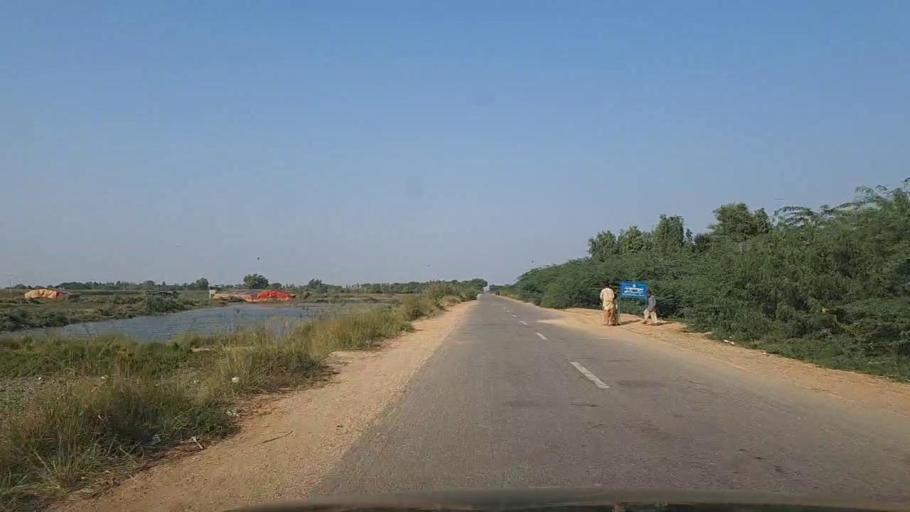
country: PK
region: Sindh
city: Thatta
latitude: 24.6184
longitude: 68.0516
